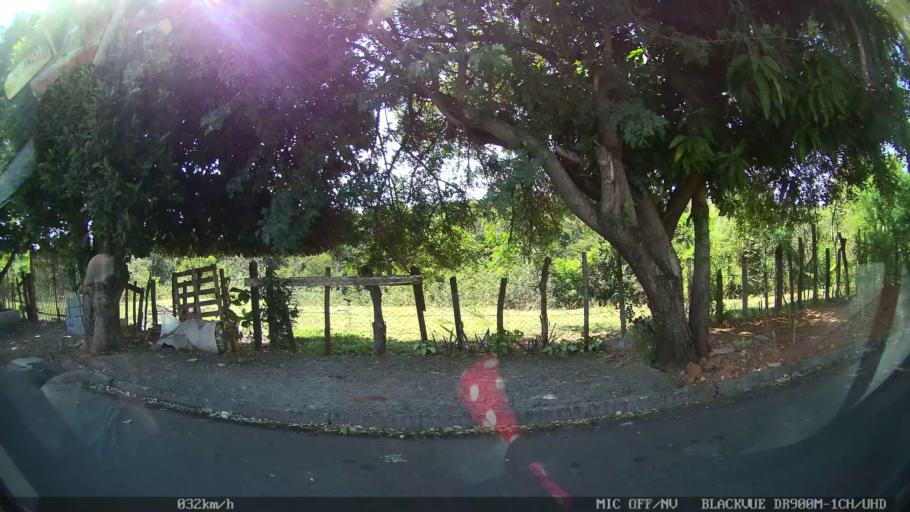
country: BR
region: Sao Paulo
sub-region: Americana
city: Americana
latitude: -22.7204
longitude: -47.3037
